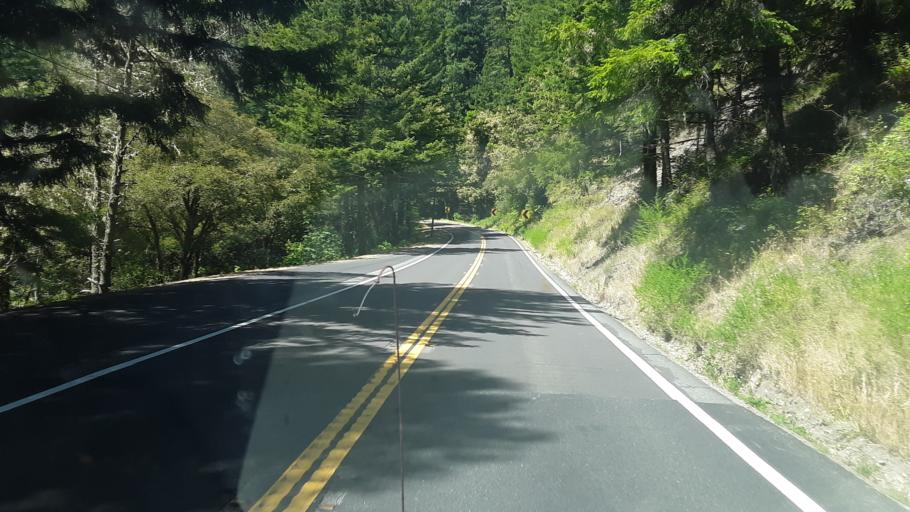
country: US
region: California
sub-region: Del Norte County
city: Bertsch-Oceanview
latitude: 41.8091
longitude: -124.0499
